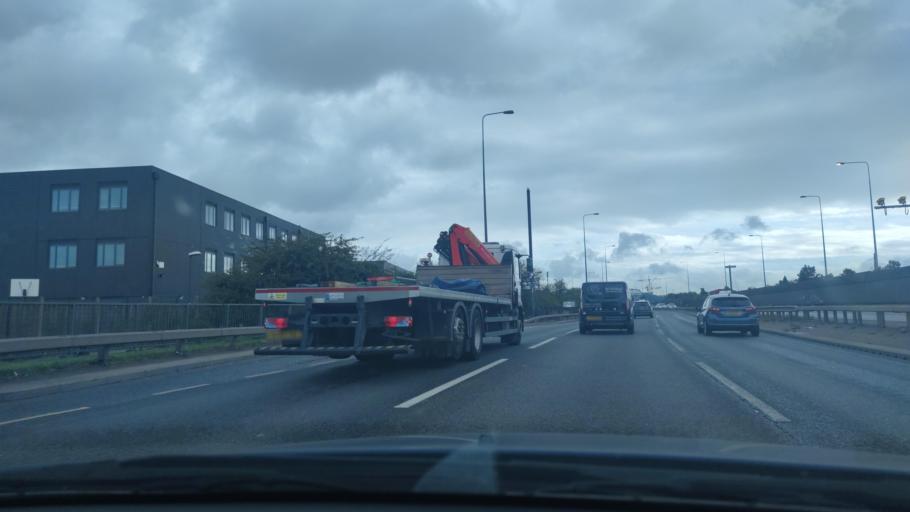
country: GB
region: England
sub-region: Greater London
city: Becontree
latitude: 51.5320
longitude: 0.1292
